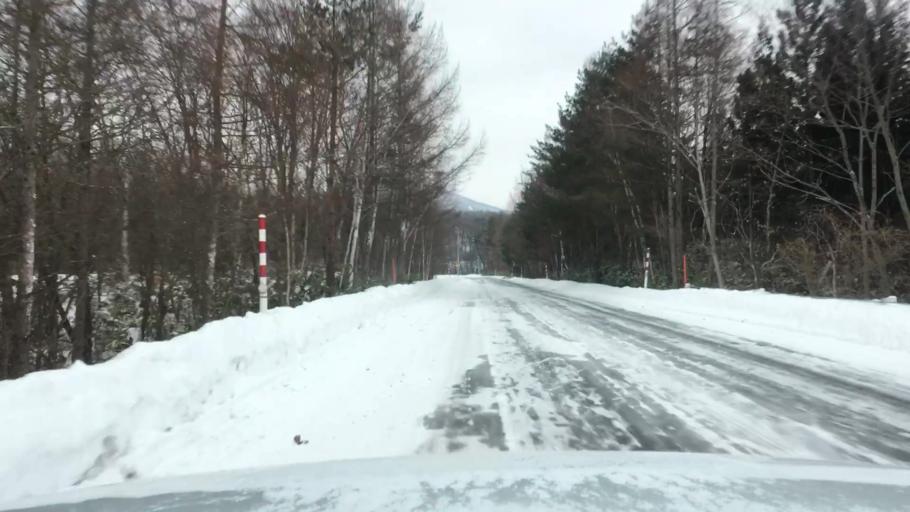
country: JP
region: Iwate
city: Shizukuishi
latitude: 39.9373
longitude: 141.0015
